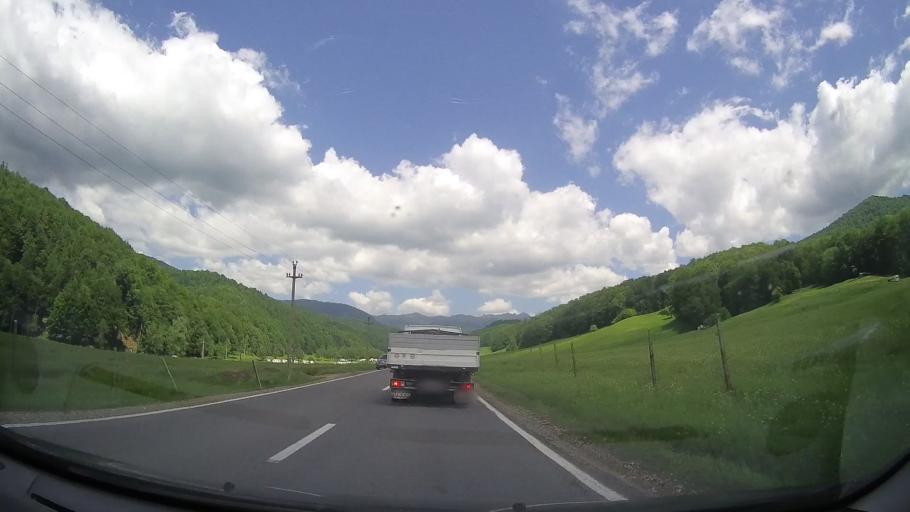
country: RO
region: Prahova
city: Maneciu
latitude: 45.4208
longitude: 25.9428
